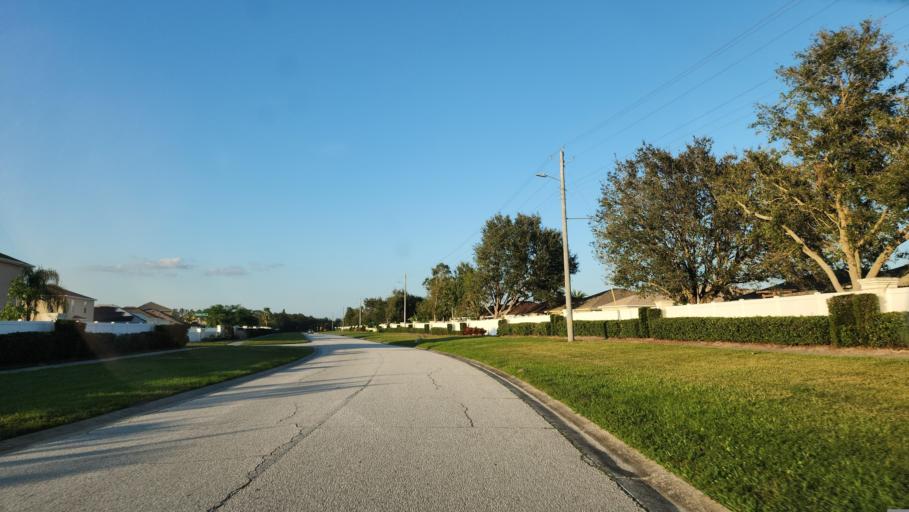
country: US
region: Florida
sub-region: Hillsborough County
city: Balm
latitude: 27.8003
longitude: -82.3038
